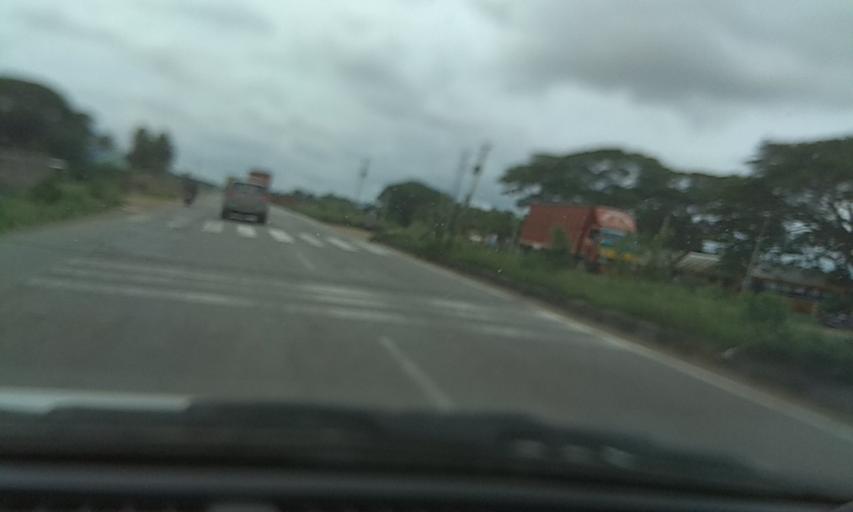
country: IN
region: Karnataka
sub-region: Davanagere
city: Mayakonda
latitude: 14.3178
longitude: 76.2390
